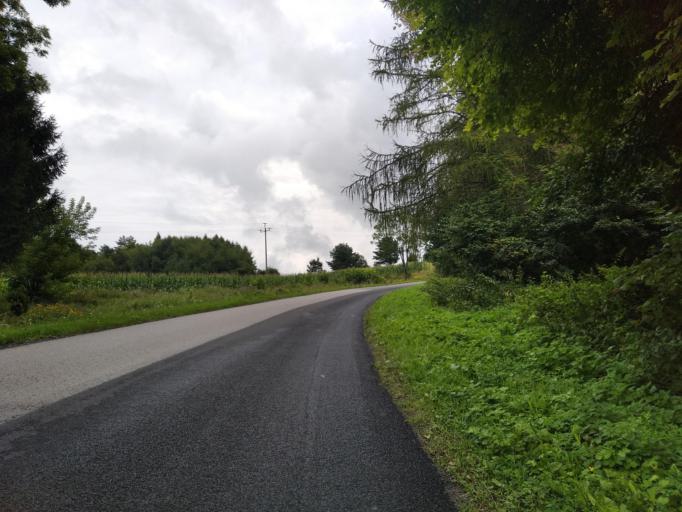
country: PL
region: Subcarpathian Voivodeship
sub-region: Powiat rzeszowski
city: Dynow
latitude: 49.7300
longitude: 22.2997
